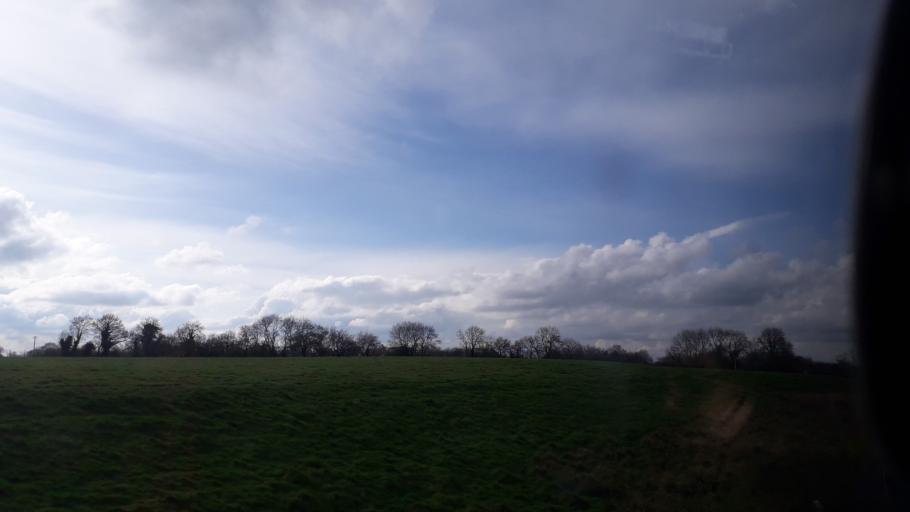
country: IE
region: Leinster
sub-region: An Mhi
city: Longwood
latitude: 53.4558
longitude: -6.9627
